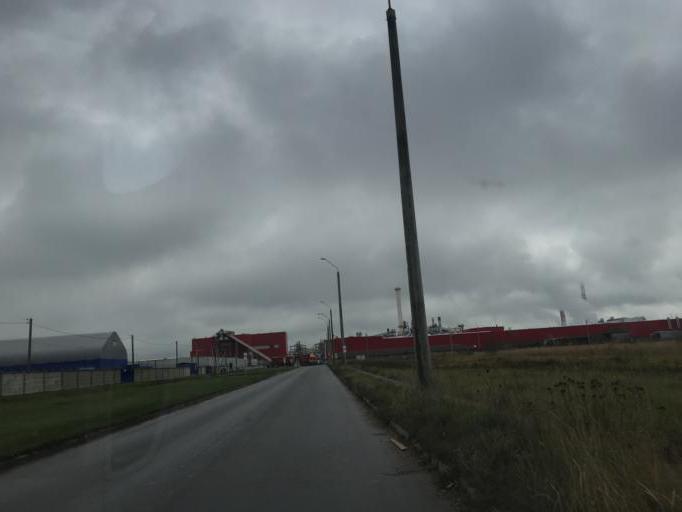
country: BY
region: Mogilev
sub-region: Mahilyowski Rayon
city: Veyno
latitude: 53.8253
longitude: 30.3525
